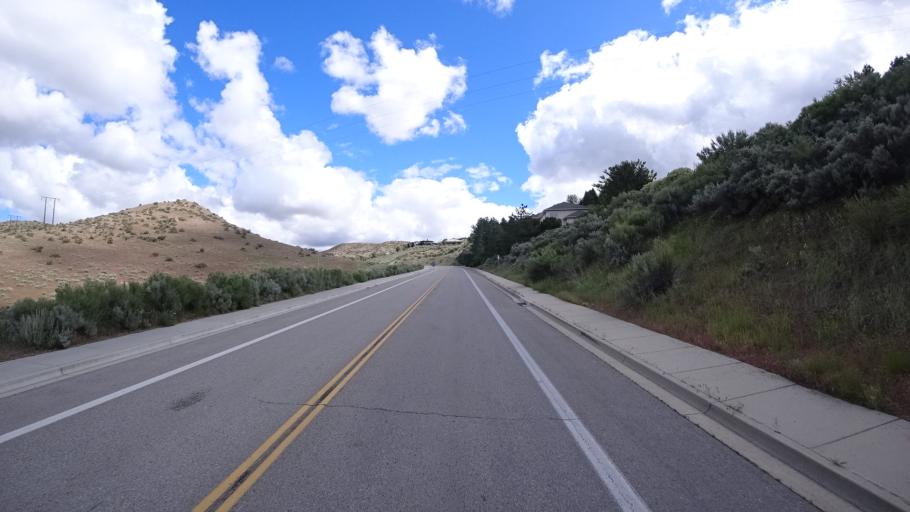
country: US
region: Idaho
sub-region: Ada County
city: Boise
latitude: 43.6534
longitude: -116.1917
